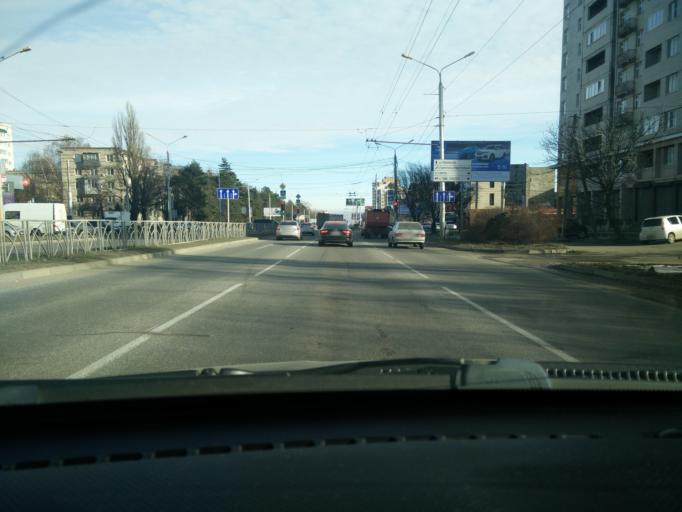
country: RU
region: Stavropol'skiy
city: Stavropol'
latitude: 45.0330
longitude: 41.9510
